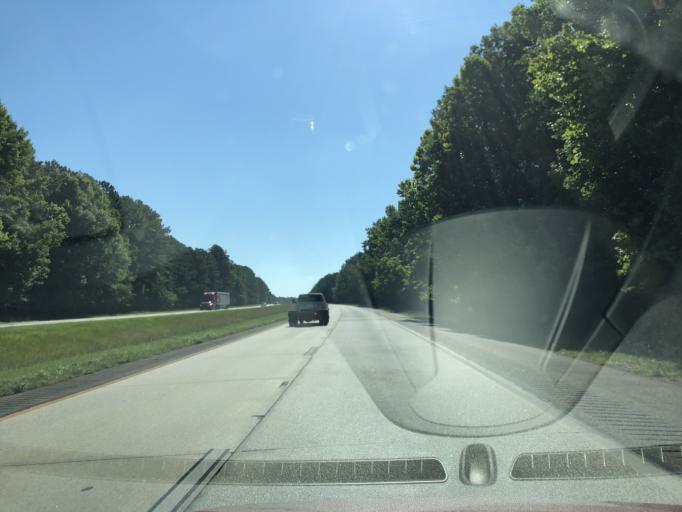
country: US
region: Georgia
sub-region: Warren County
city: Firing Range
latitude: 33.5006
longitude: -82.7823
